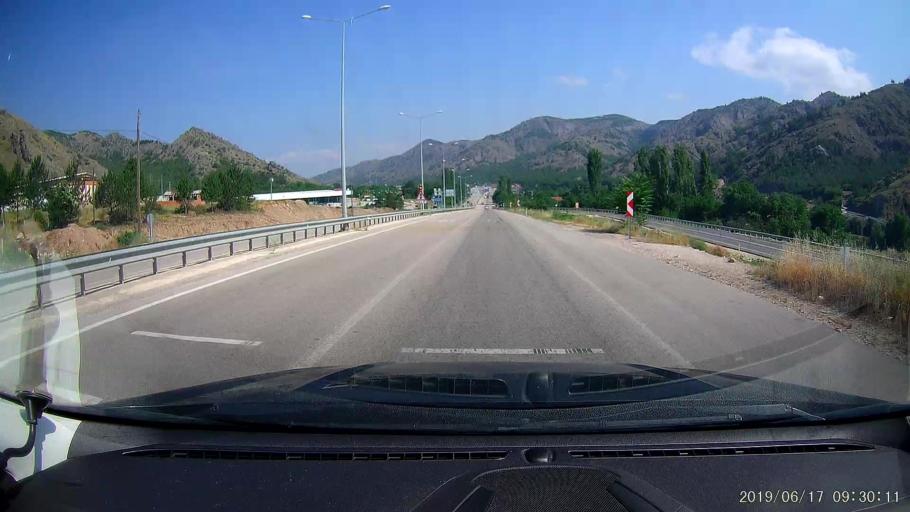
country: TR
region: Amasya
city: Amasya
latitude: 40.7033
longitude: 35.8052
